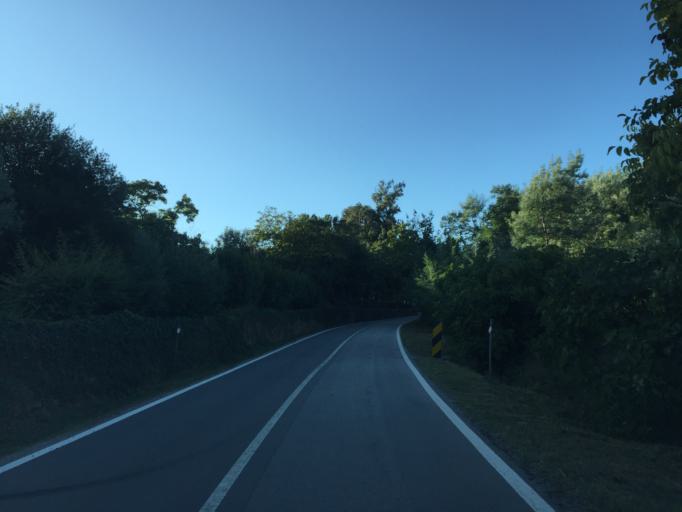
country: PT
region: Portalegre
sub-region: Castelo de Vide
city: Castelo de Vide
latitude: 39.4022
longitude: -7.4377
